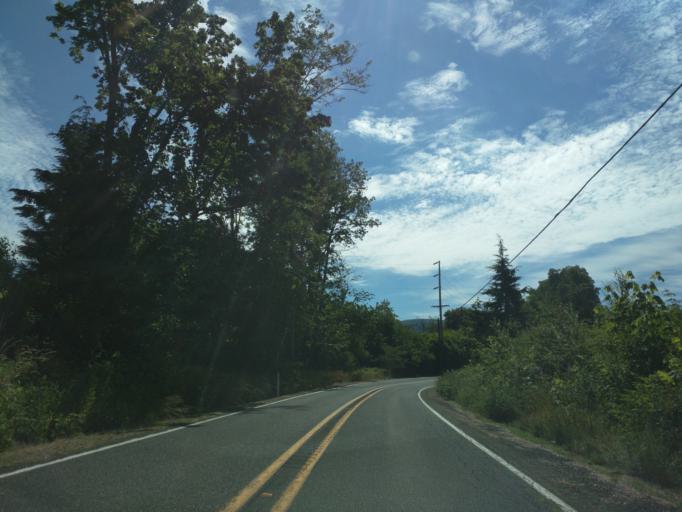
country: US
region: Washington
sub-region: Whatcom County
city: Peaceful Valley
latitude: 48.9762
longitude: -122.1771
